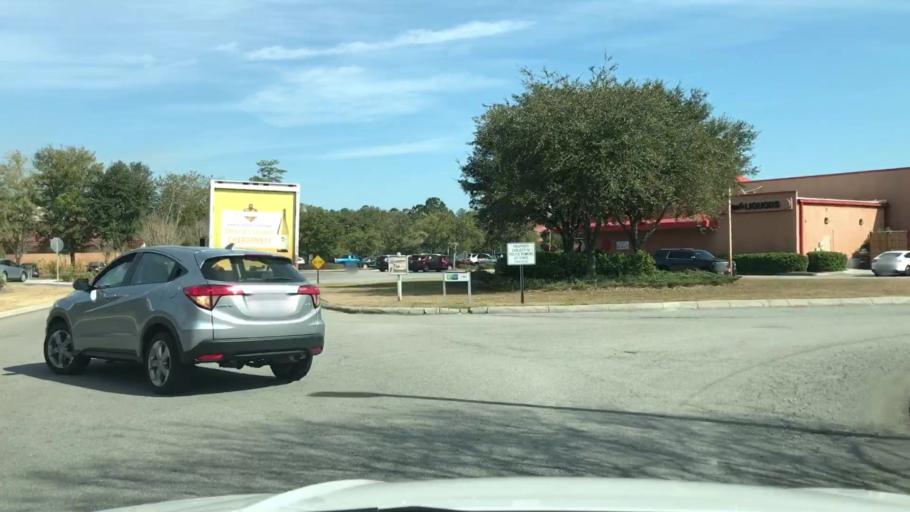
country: US
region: South Carolina
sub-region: Beaufort County
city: Bluffton
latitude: 32.2569
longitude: -80.8532
